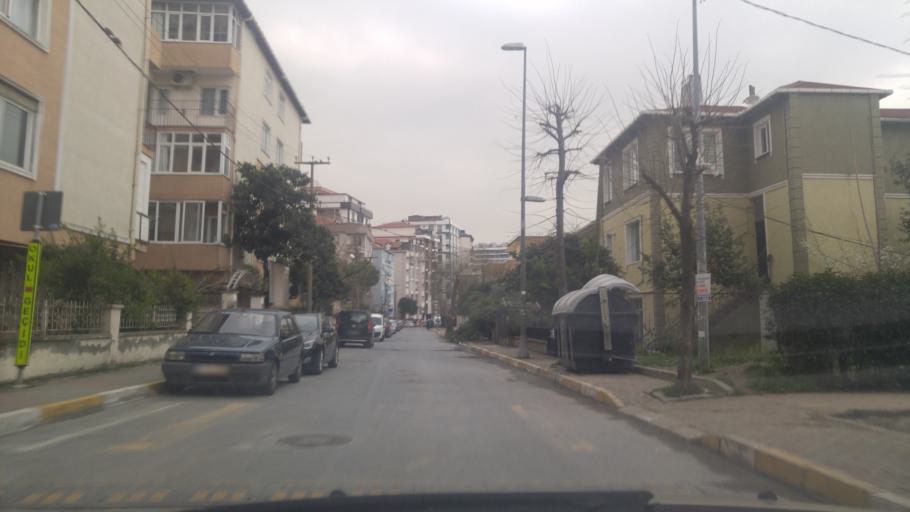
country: TR
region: Istanbul
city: Mahmutbey
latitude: 40.9966
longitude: 28.7645
